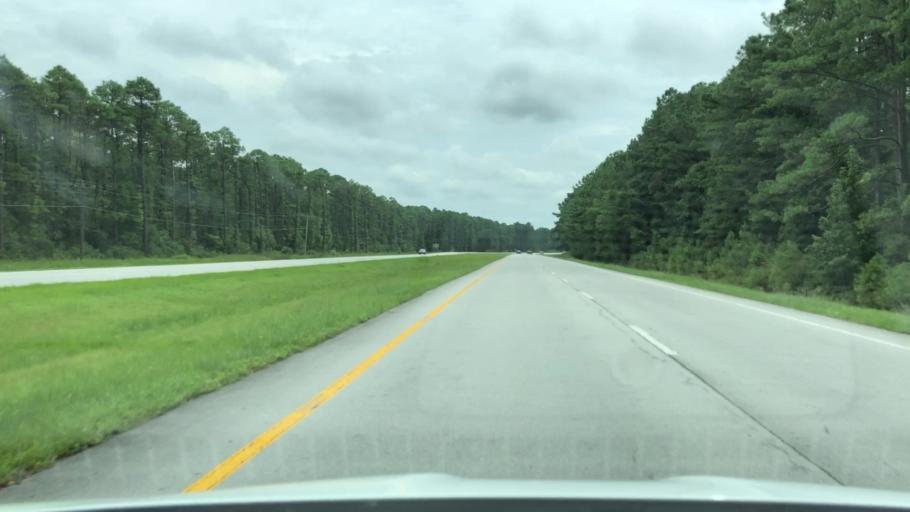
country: US
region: North Carolina
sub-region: Craven County
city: Havelock
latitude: 34.8489
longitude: -76.8866
